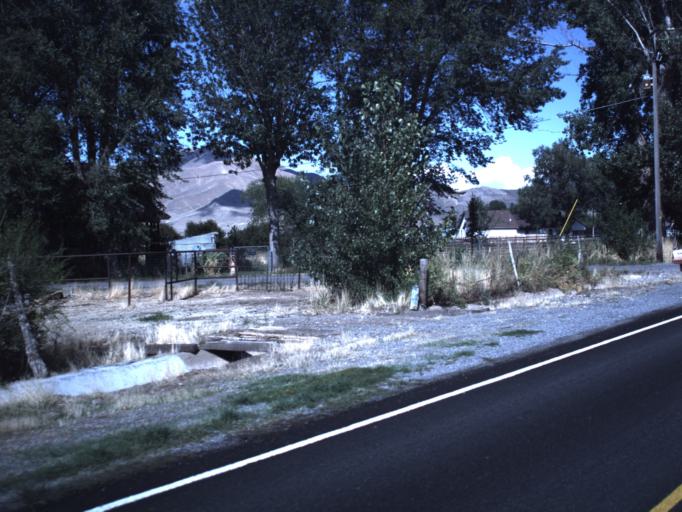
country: US
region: Utah
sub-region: Utah County
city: Genola
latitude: 39.9924
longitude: -111.8301
